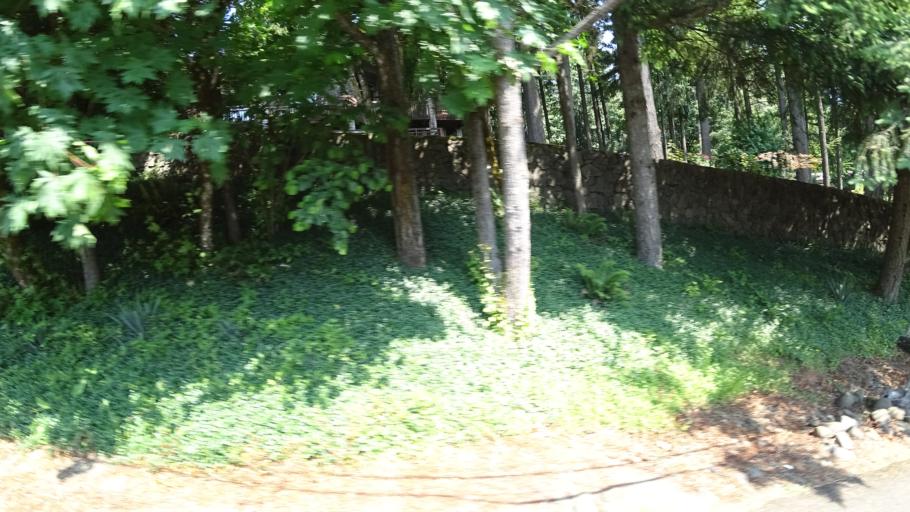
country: US
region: Oregon
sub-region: Clackamas County
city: Happy Valley
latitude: 45.4461
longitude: -122.5561
